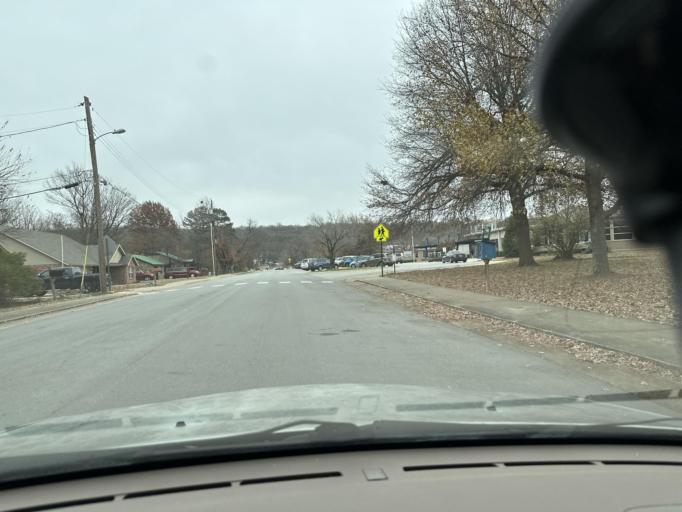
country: US
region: Arkansas
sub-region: Washington County
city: Fayetteville
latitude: 36.0886
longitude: -94.1585
